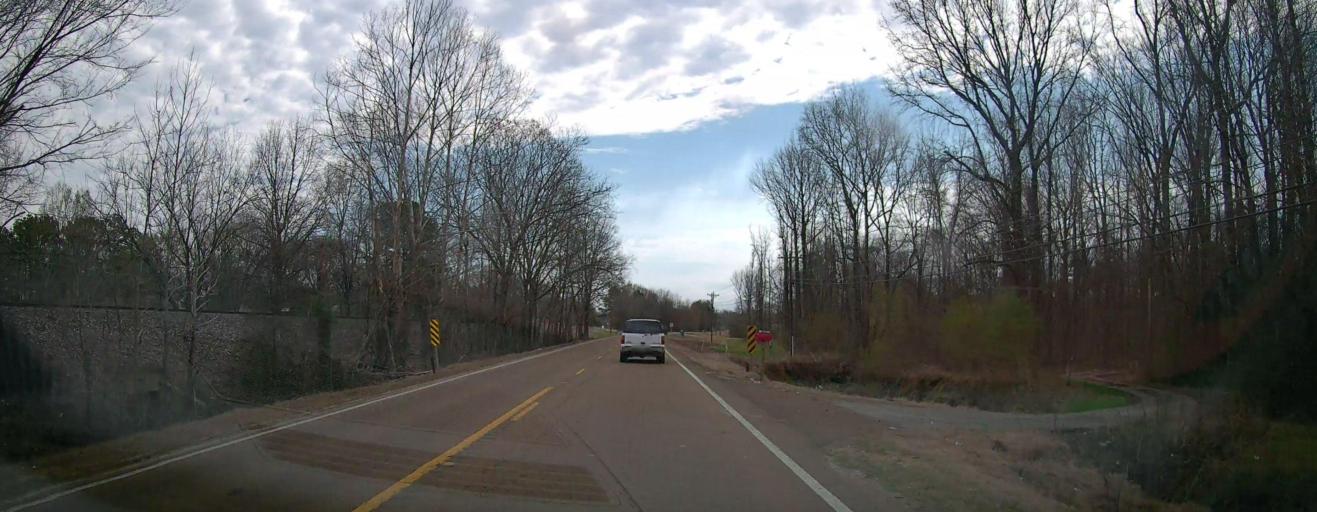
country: US
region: Mississippi
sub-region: Marshall County
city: Byhalia
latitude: 34.8799
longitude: -89.7092
